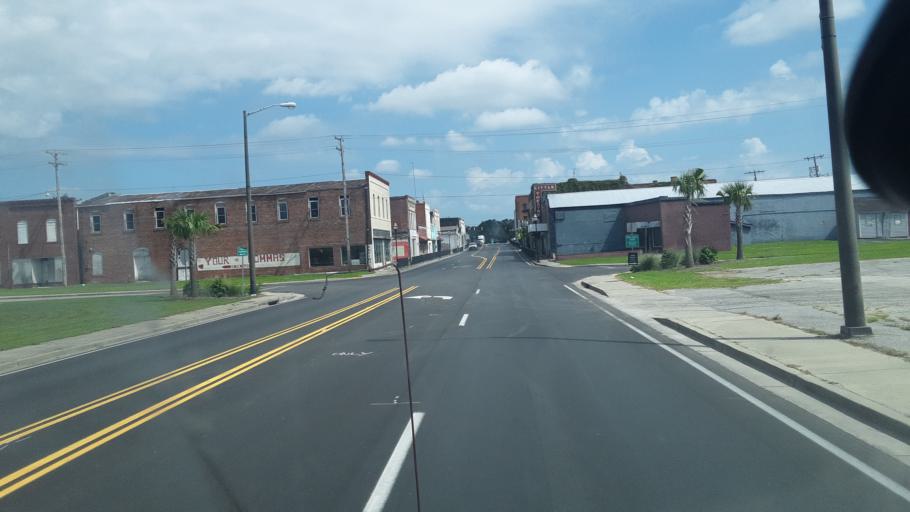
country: US
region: South Carolina
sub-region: Bamberg County
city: Bamberg
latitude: 33.2945
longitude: -81.0359
